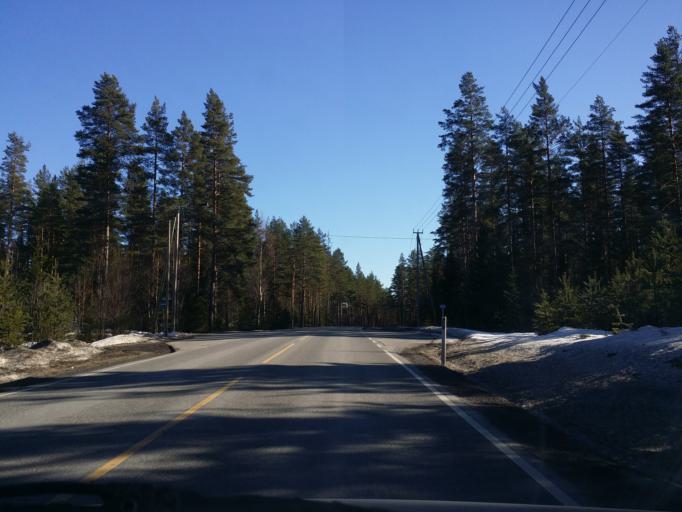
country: NO
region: Buskerud
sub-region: Ringerike
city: Honefoss
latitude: 60.3167
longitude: 10.1463
